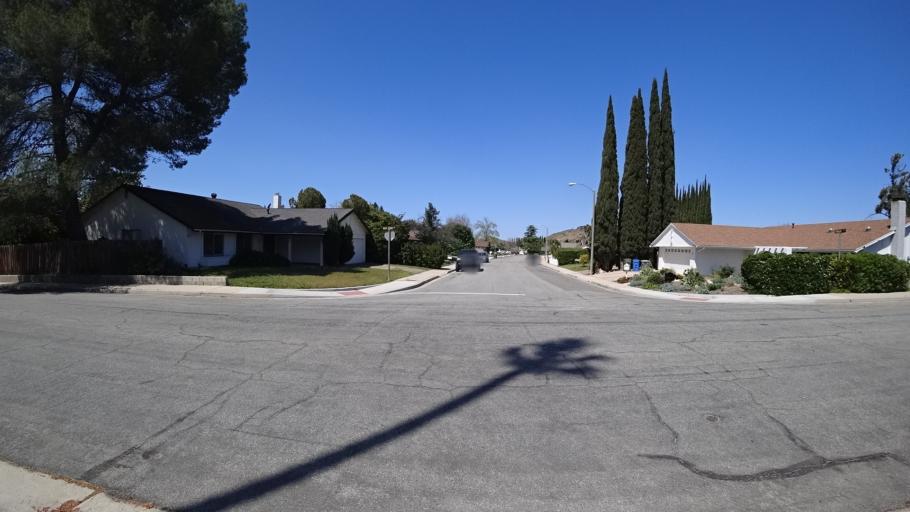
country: US
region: California
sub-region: Ventura County
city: Casa Conejo
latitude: 34.2125
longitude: -118.8894
